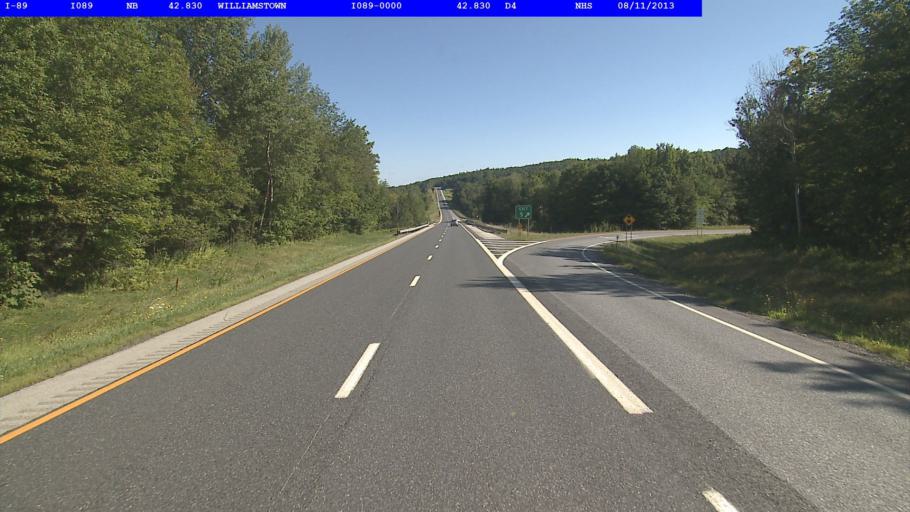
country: US
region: Vermont
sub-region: Washington County
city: Northfield
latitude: 44.1135
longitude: -72.6085
